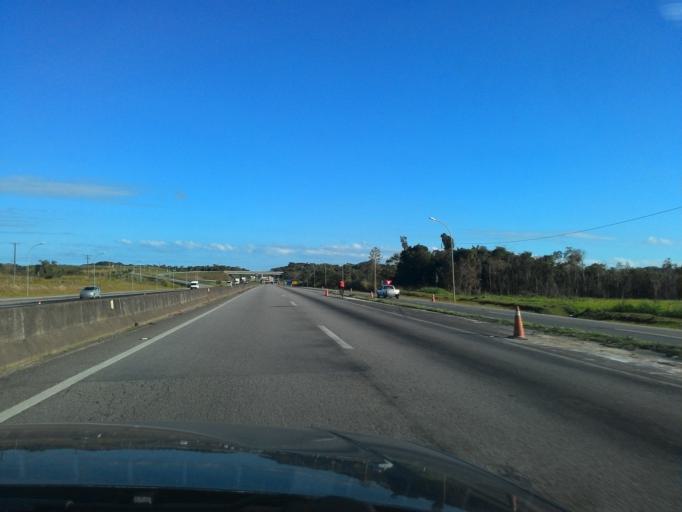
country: BR
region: Sao Paulo
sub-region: Registro
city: Registro
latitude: -24.5341
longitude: -47.8581
